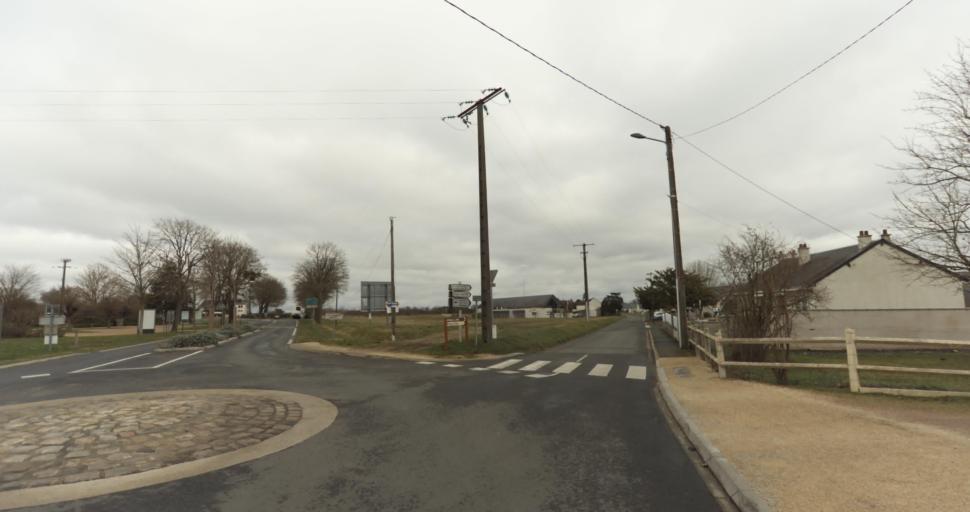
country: FR
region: Pays de la Loire
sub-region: Departement de Maine-et-Loire
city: Montreuil-Bellay
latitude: 47.1413
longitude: -0.1539
